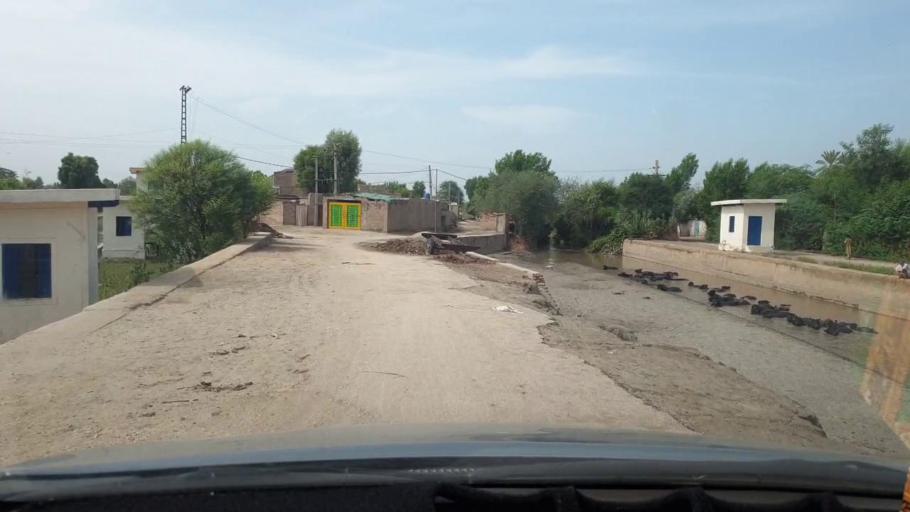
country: PK
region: Sindh
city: Khairpur
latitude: 27.5131
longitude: 68.7605
